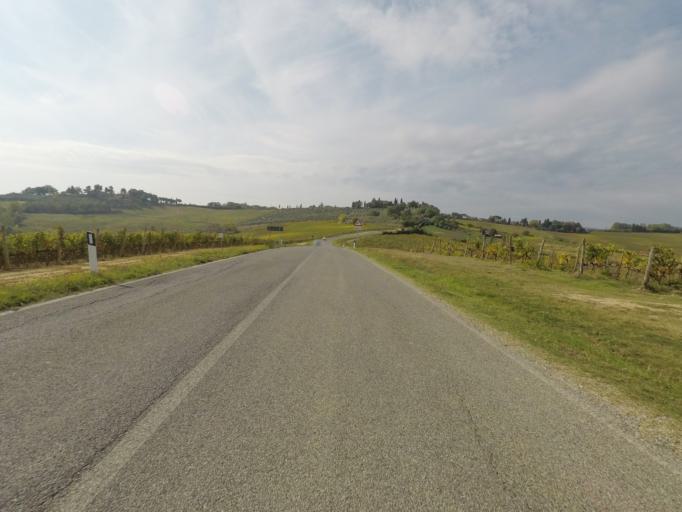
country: IT
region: Tuscany
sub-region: Provincia di Siena
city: Belverde
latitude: 43.3625
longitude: 11.3245
